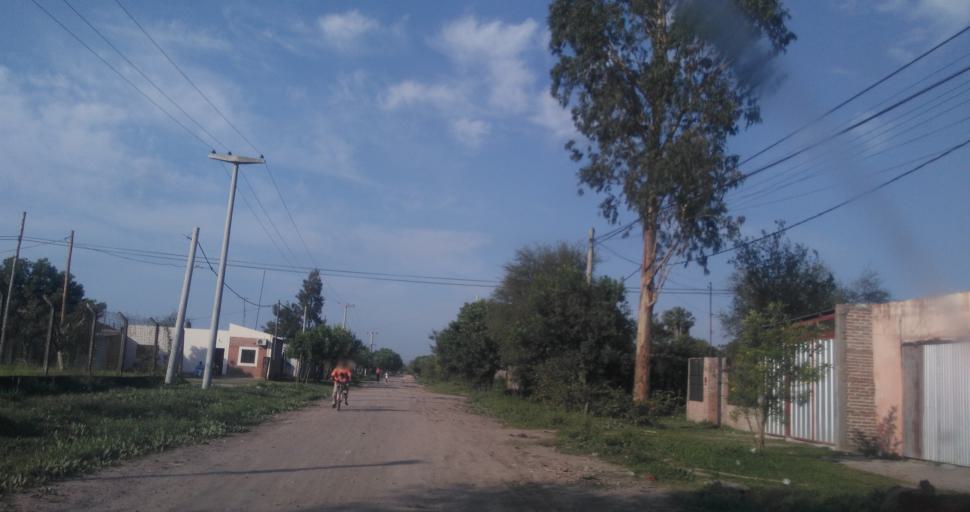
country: AR
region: Chaco
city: Resistencia
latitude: -27.4804
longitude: -59.0032
